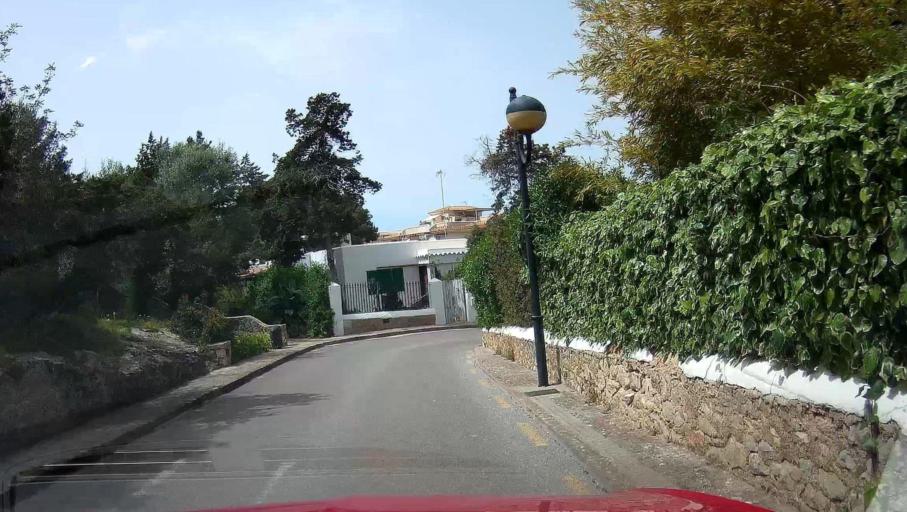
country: ES
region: Balearic Islands
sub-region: Illes Balears
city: Santa Eularia des Riu
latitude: 38.9844
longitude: 1.5303
